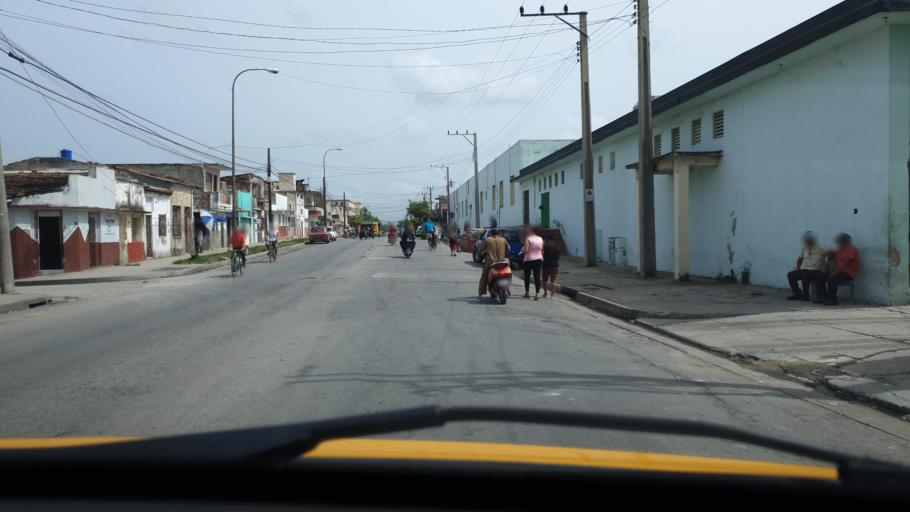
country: CU
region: Villa Clara
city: Santa Clara
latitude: 22.3962
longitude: -79.9625
